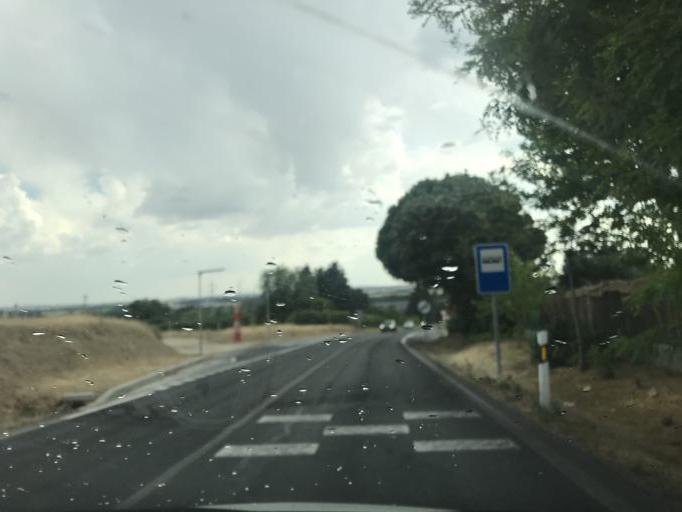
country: ES
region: Madrid
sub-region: Provincia de Madrid
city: Paracuellos de Jarama
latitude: 40.5022
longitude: -3.5413
